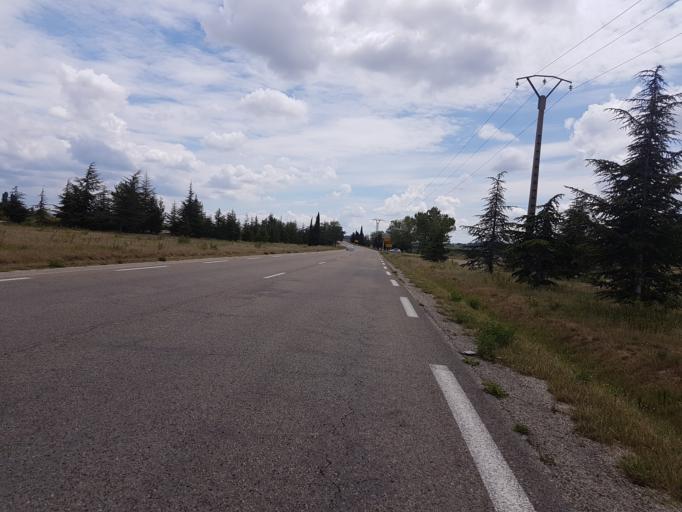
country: FR
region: Languedoc-Roussillon
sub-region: Departement du Gard
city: Vallabregues
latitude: 43.8461
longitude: 4.6199
